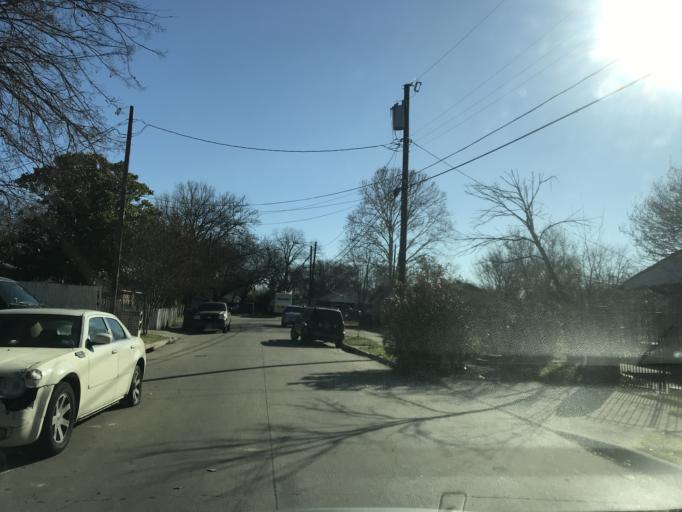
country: US
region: Texas
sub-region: Dallas County
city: Cockrell Hill
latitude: 32.7751
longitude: -96.9140
